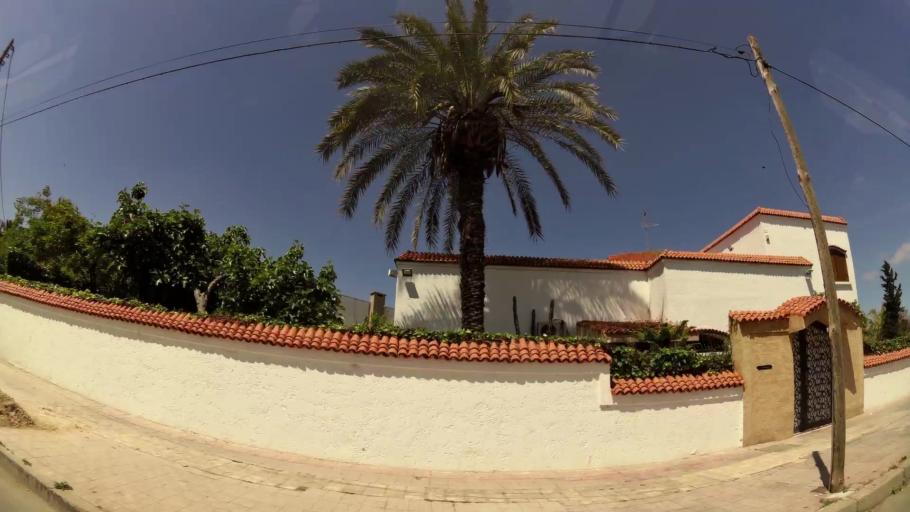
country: MA
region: Fes-Boulemane
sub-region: Fes
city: Fes
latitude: 34.0287
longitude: -5.0144
